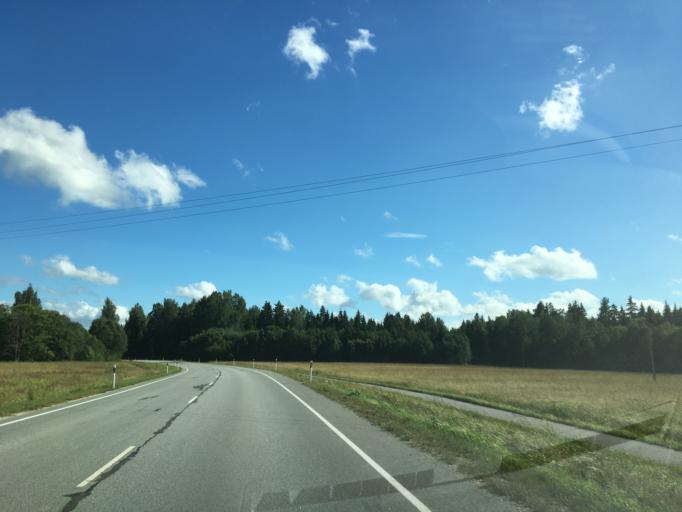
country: EE
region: Paernumaa
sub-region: Vaendra vald (alev)
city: Vandra
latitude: 58.6300
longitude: 25.1001
